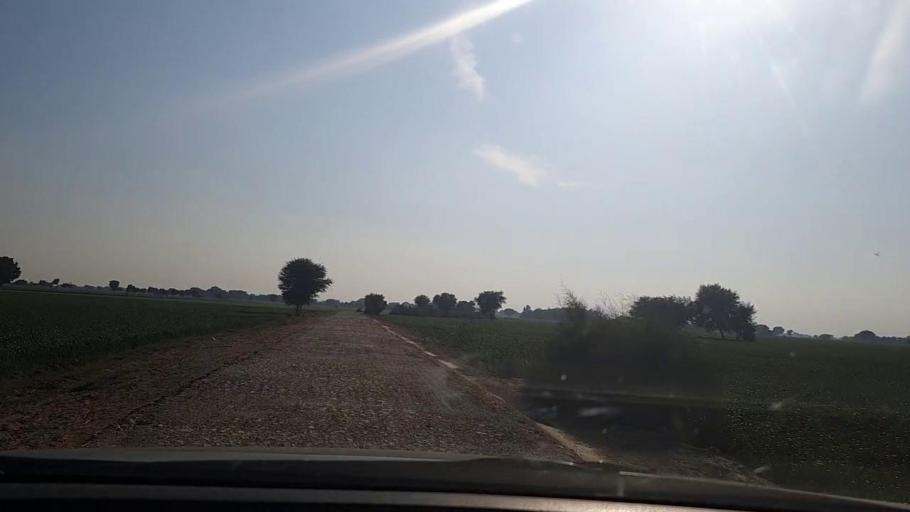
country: PK
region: Sindh
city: Sehwan
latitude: 26.3145
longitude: 68.0035
